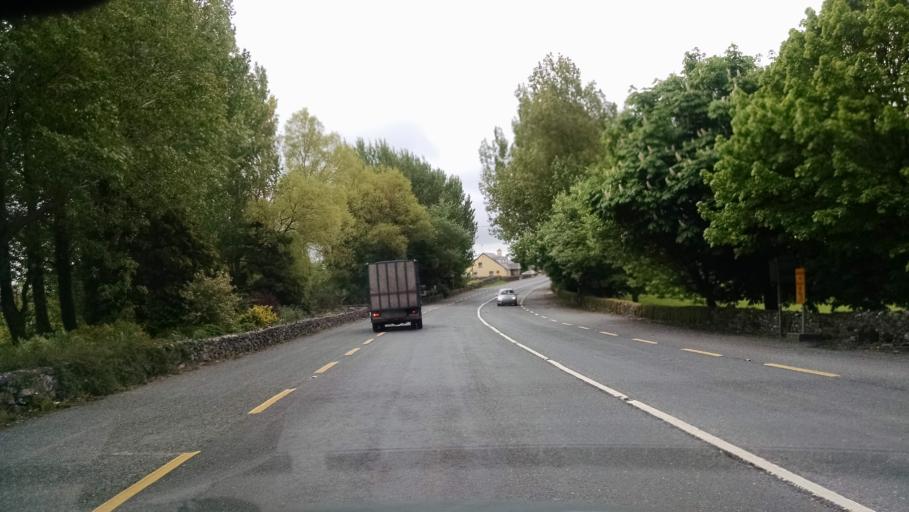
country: IE
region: Connaught
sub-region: County Galway
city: Moycullen
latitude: 53.4662
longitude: -9.1051
